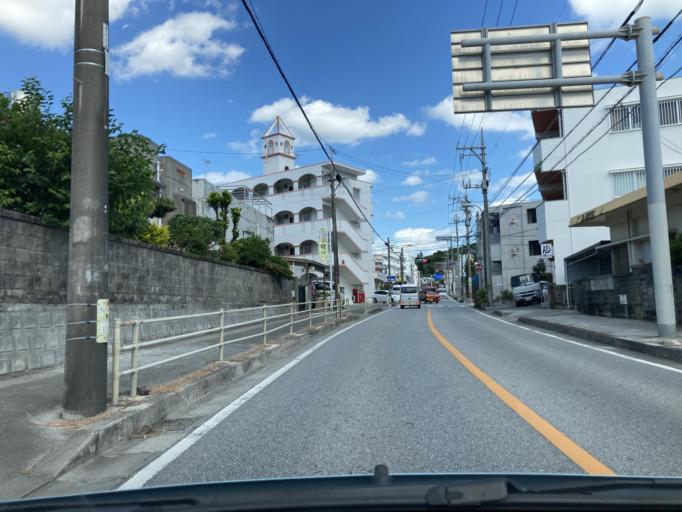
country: JP
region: Okinawa
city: Tomigusuku
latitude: 26.1881
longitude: 127.7281
